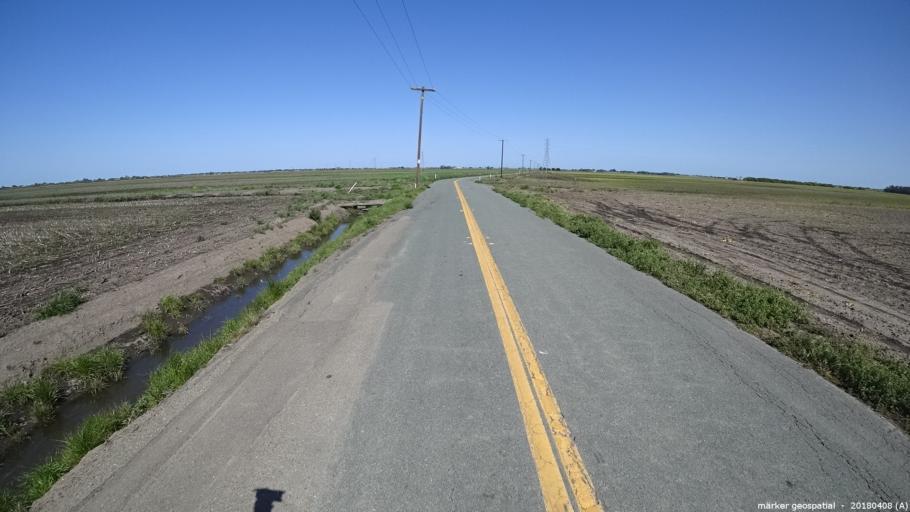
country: US
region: California
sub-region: Sacramento County
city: Walnut Grove
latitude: 38.3065
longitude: -121.5527
